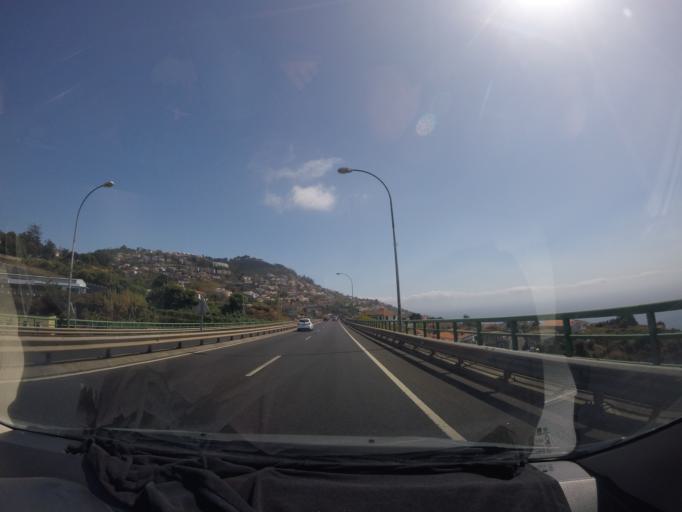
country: PT
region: Madeira
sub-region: Funchal
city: Nossa Senhora do Monte
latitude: 32.6565
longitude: -16.8848
